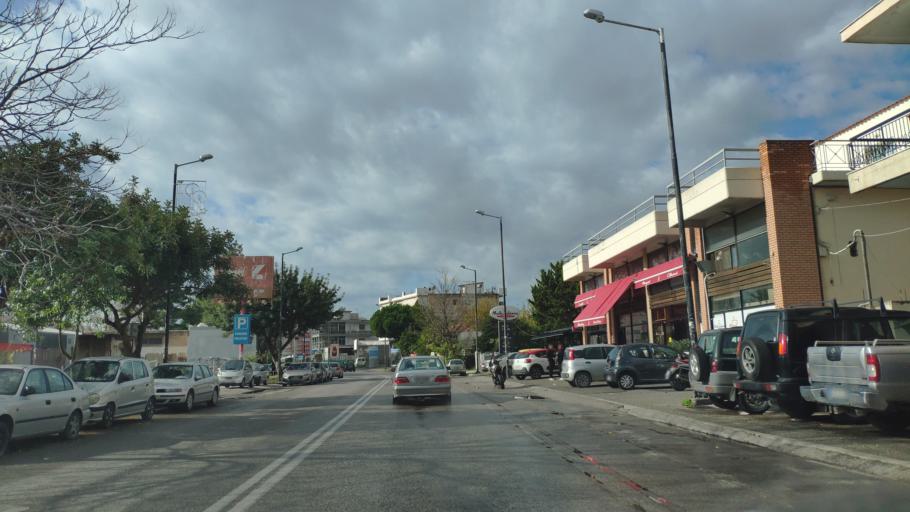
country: GR
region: Attica
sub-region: Nomarchia Dytikis Attikis
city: Elefsina
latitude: 38.0456
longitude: 23.5466
